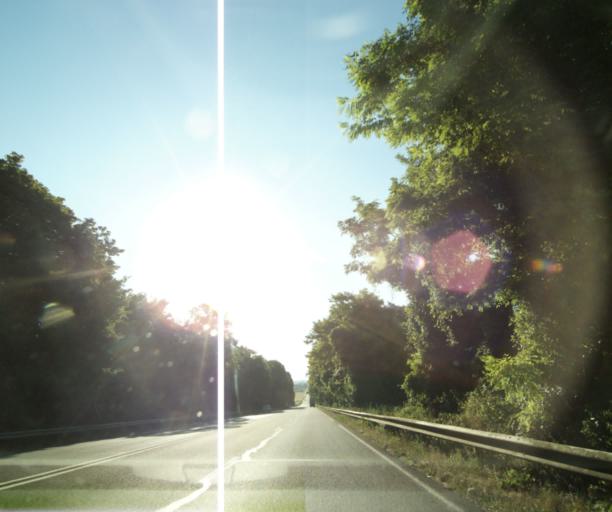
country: FR
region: Ile-de-France
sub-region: Departement de Seine-et-Marne
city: Vernou-la-Celle-sur-Seine
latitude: 48.3613
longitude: 2.8685
